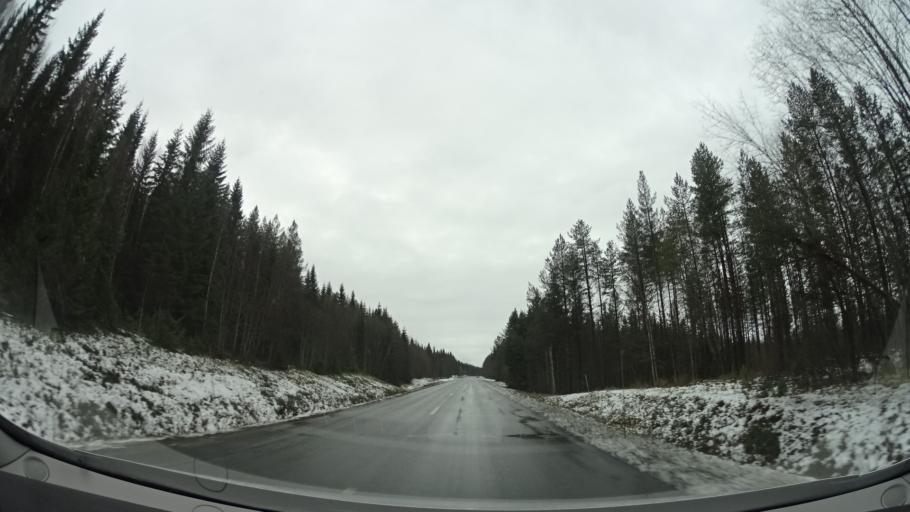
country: SE
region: Jaemtland
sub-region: Stroemsunds Kommun
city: Stroemsund
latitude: 64.0190
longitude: 15.5249
